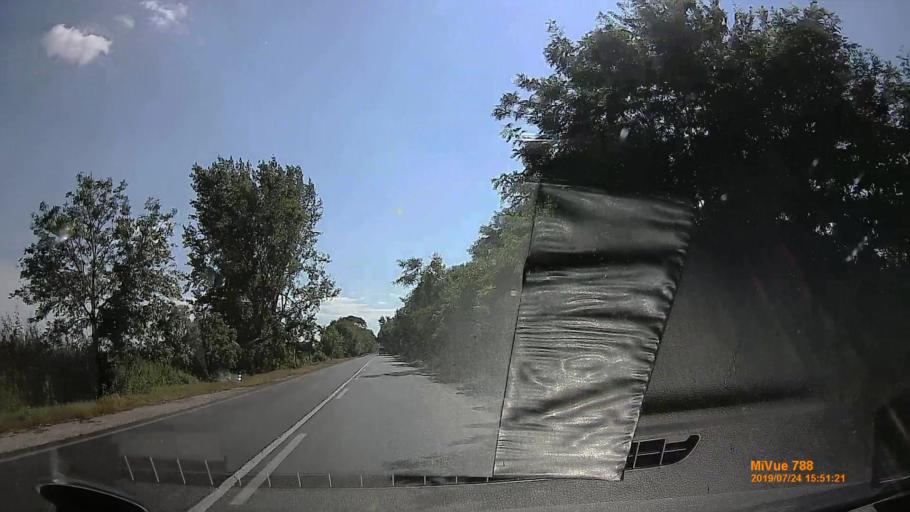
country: HU
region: Szabolcs-Szatmar-Bereg
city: Nyirmada
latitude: 48.0413
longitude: 22.1844
